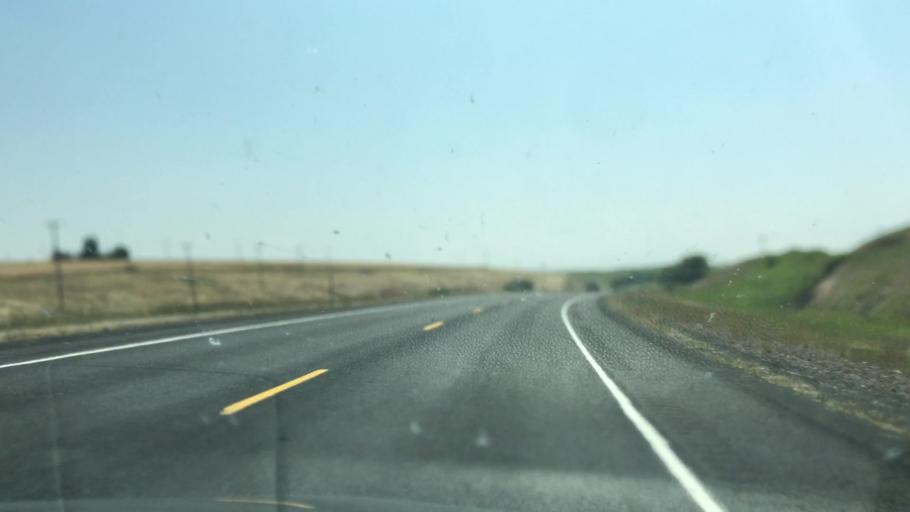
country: US
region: Idaho
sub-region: Lewis County
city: Nezperce
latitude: 46.2260
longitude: -116.4403
